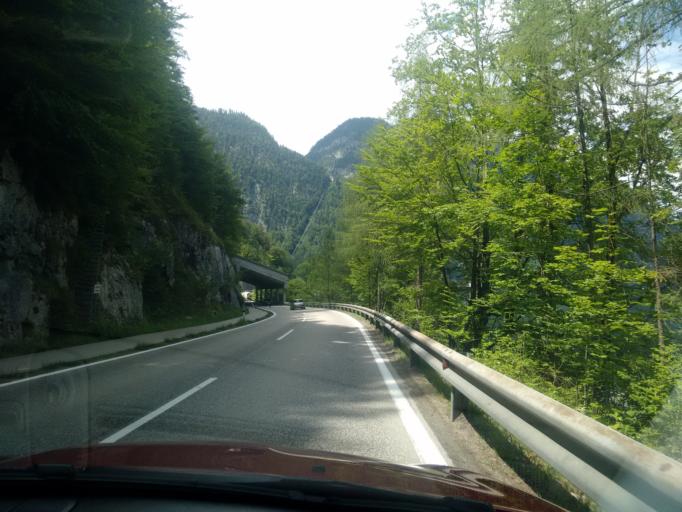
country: AT
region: Upper Austria
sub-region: Politischer Bezirk Gmunden
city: Bad Goisern
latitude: 47.5487
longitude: 13.6554
